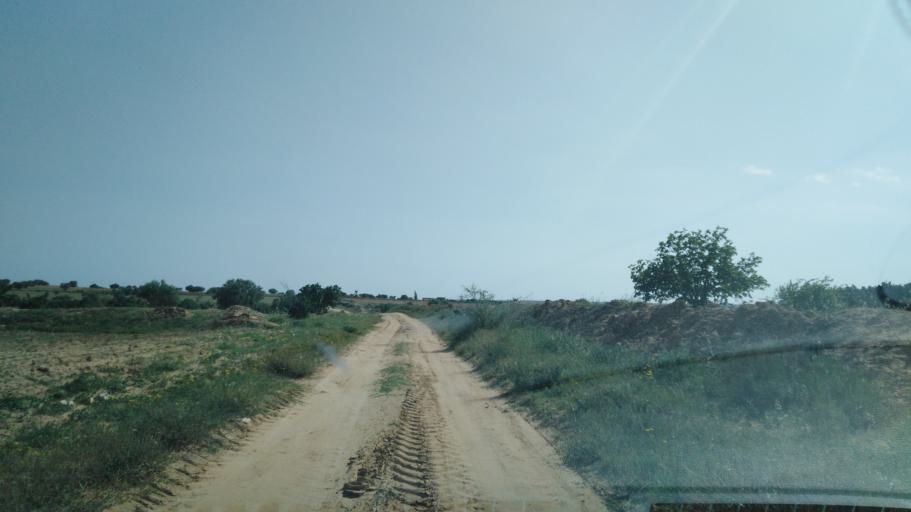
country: TN
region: Safaqis
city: Bi'r `Ali Bin Khalifah
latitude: 34.7898
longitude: 10.3706
